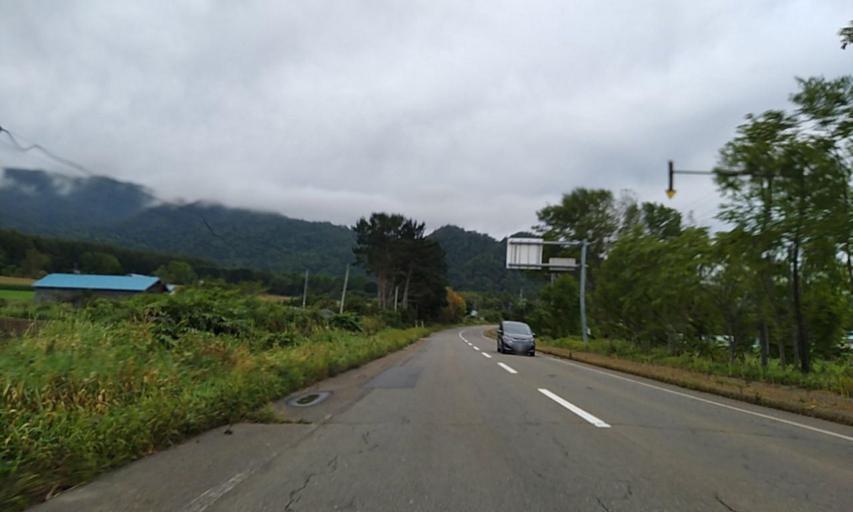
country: JP
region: Hokkaido
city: Bihoro
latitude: 43.5812
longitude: 144.2776
